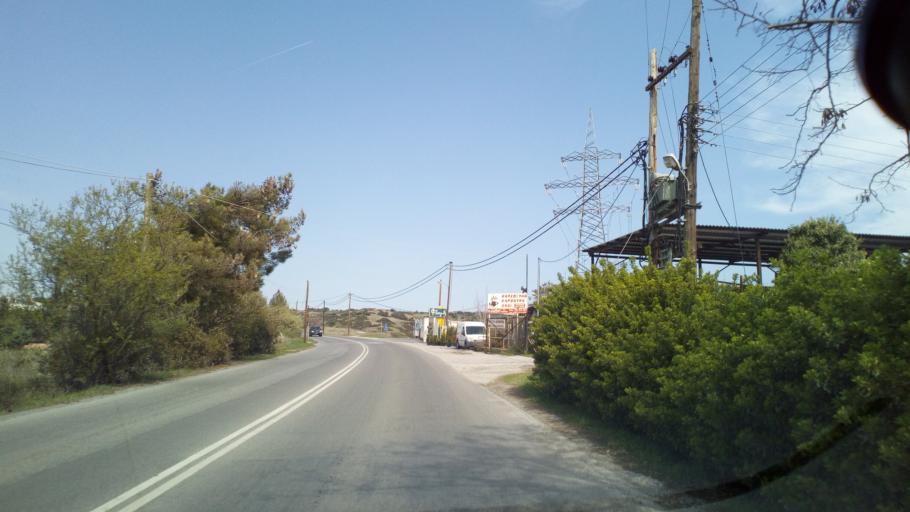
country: GR
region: Central Macedonia
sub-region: Nomos Thessalonikis
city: Thermi
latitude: 40.5630
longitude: 23.0241
